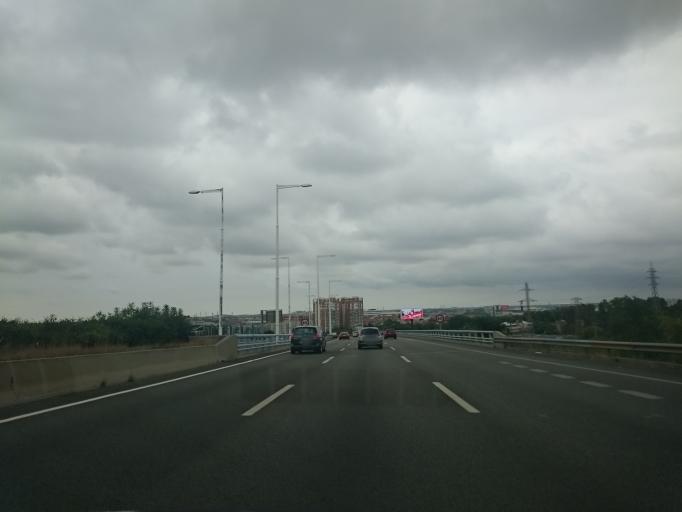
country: ES
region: Catalonia
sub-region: Provincia de Barcelona
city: L'Hospitalet de Llobregat
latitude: 41.3614
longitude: 2.0885
